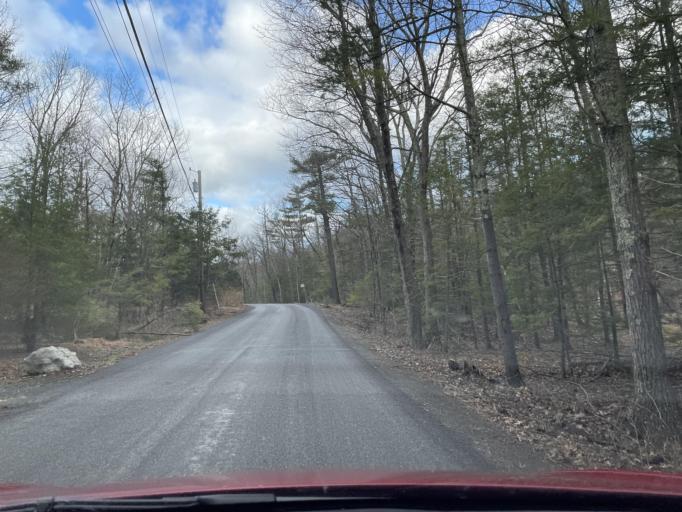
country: US
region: New York
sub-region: Ulster County
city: Zena
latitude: 42.0761
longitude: -74.0630
